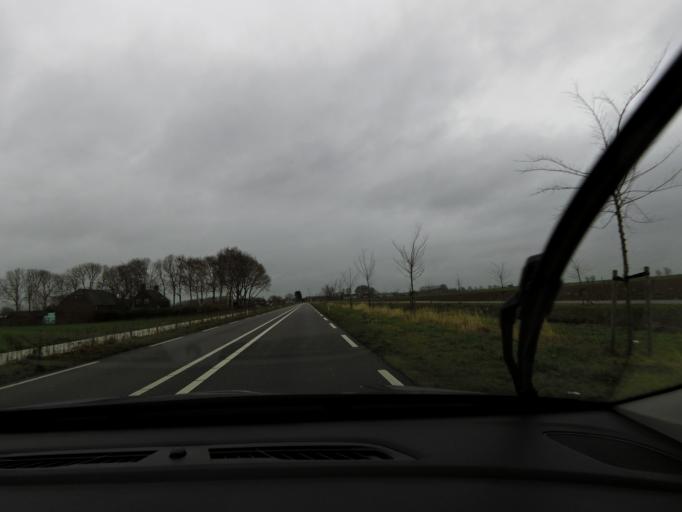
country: NL
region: North Brabant
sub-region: Gemeente Woudrichem
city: Almkerk
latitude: 51.7305
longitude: 4.9439
